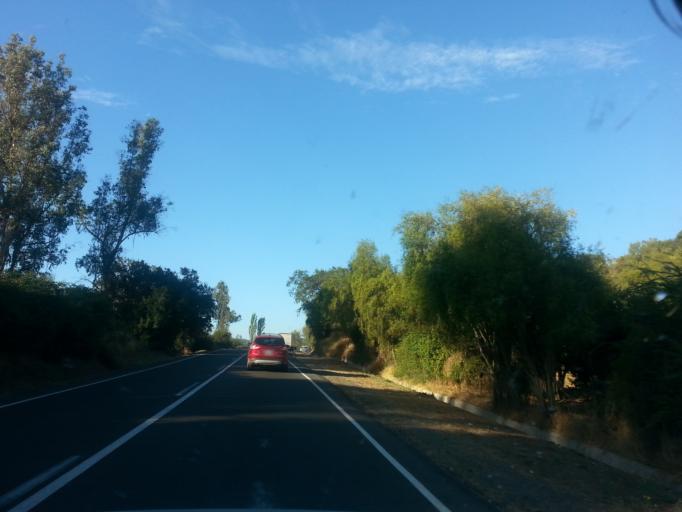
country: CL
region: Valparaiso
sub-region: Provincia de Marga Marga
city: Villa Alemana
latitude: -33.2151
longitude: -71.3890
